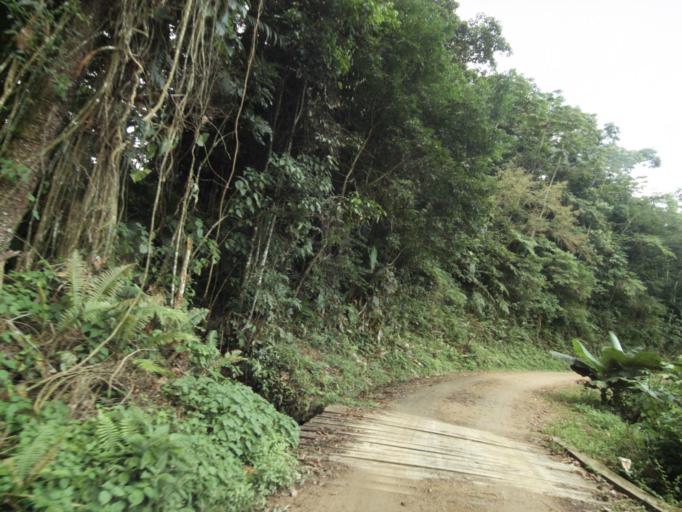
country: BR
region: Santa Catarina
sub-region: Pomerode
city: Pomerode
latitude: -26.7009
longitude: -49.2285
